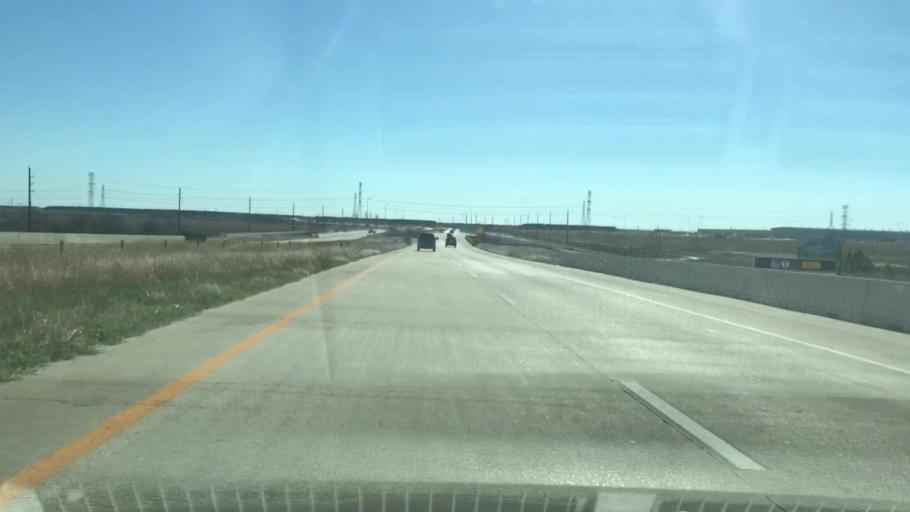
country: US
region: Texas
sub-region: Harris County
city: Cypress
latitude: 29.9209
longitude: -95.7622
